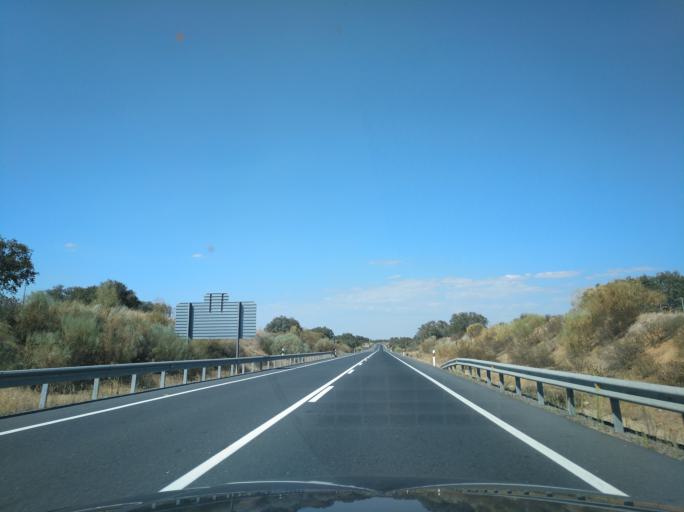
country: ES
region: Andalusia
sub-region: Provincia de Huelva
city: San Bartolome de la Torre
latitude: 37.4543
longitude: -7.1269
